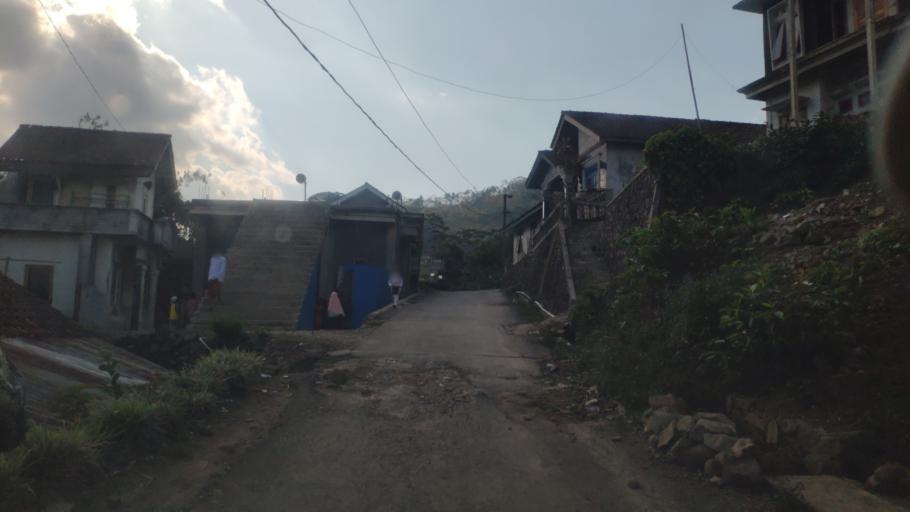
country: ID
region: Central Java
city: Buaran
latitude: -7.2347
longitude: 109.5709
